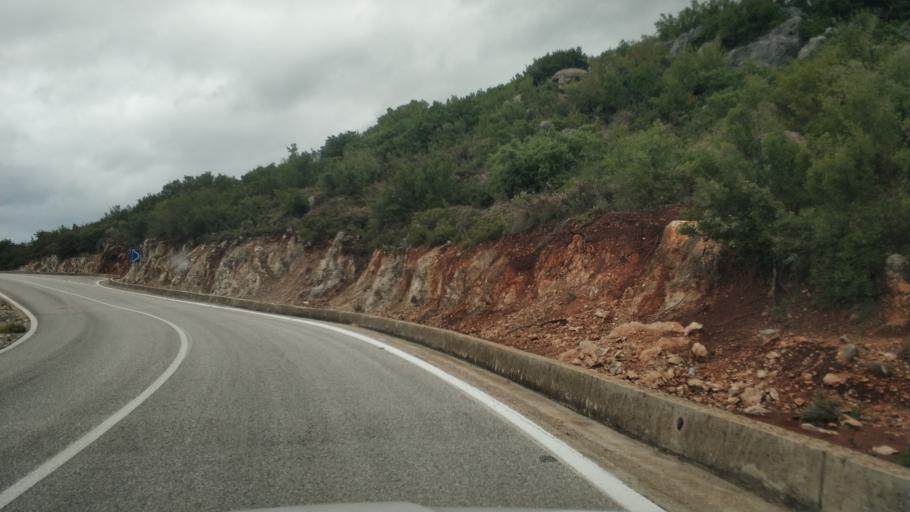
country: AL
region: Vlore
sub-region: Rrethi i Vlores
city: Vranisht
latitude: 40.1425
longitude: 19.6668
